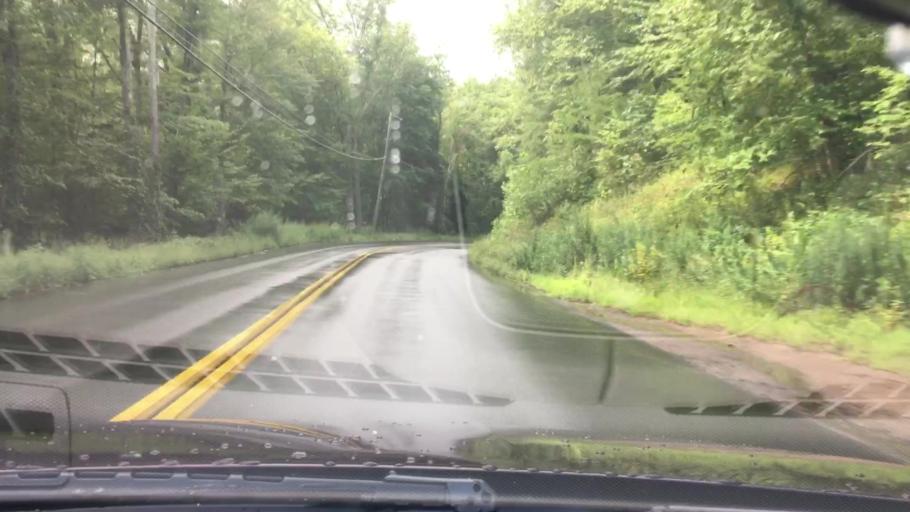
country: US
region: Connecticut
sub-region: Hartford County
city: Manchester
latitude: 41.7311
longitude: -72.5351
